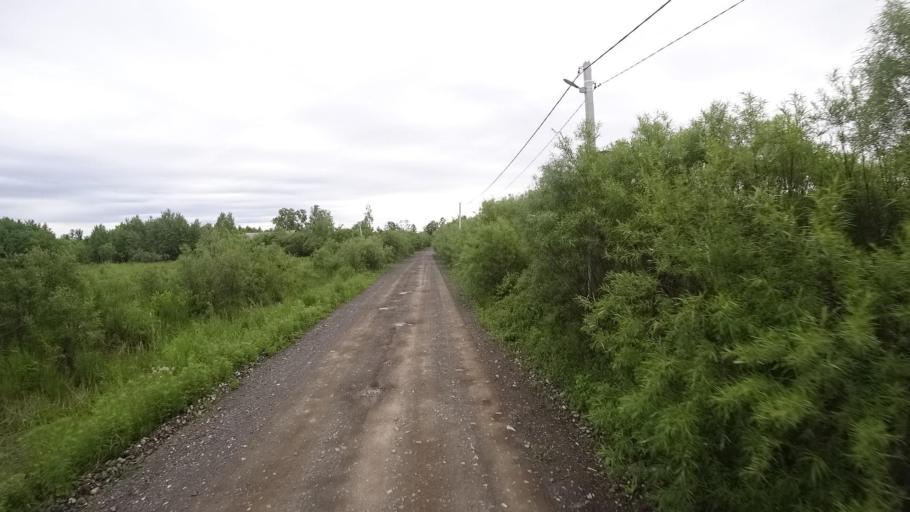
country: RU
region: Khabarovsk Krai
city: Amursk
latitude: 49.9082
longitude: 136.1488
